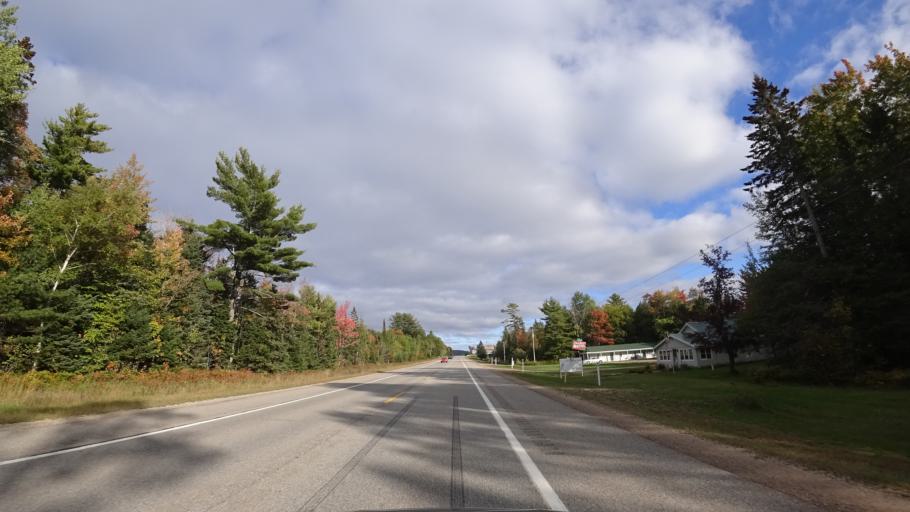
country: US
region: Michigan
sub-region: Alger County
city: Munising
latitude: 46.4411
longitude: -86.7246
